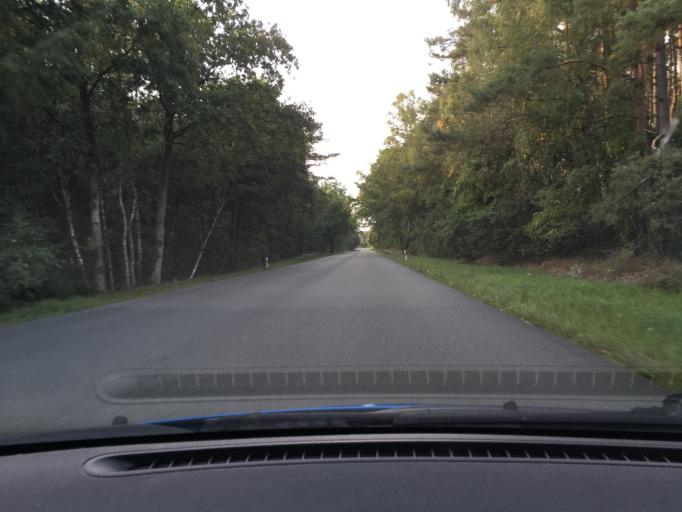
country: DE
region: Lower Saxony
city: Munster
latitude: 52.9133
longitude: 10.0830
